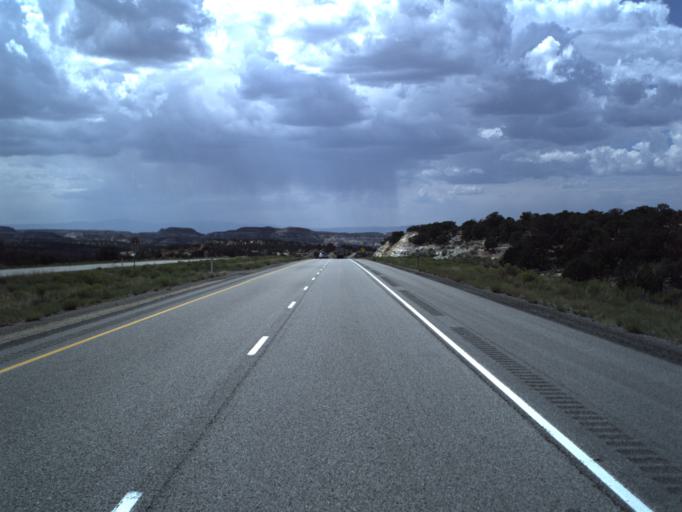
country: US
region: Utah
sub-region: Emery County
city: Ferron
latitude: 38.8593
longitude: -110.8277
